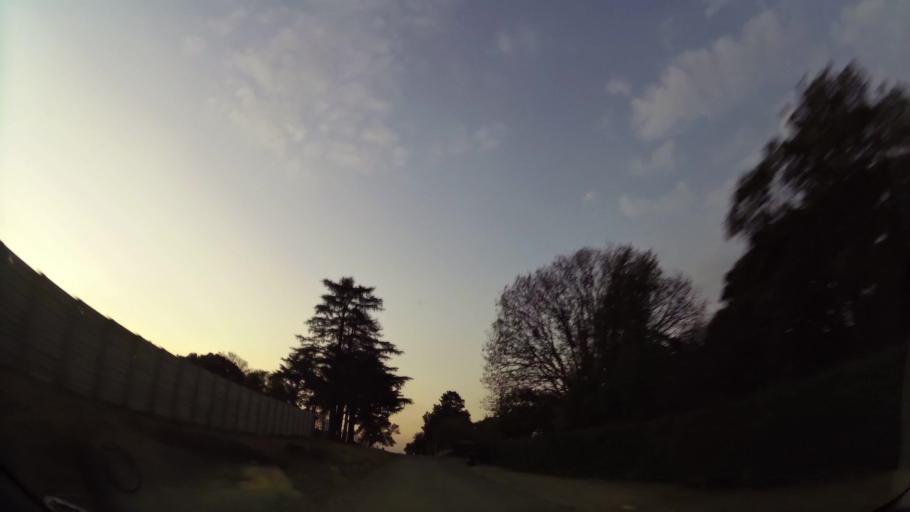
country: ZA
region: Gauteng
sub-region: Ekurhuleni Metropolitan Municipality
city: Benoni
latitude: -26.1210
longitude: 28.3052
